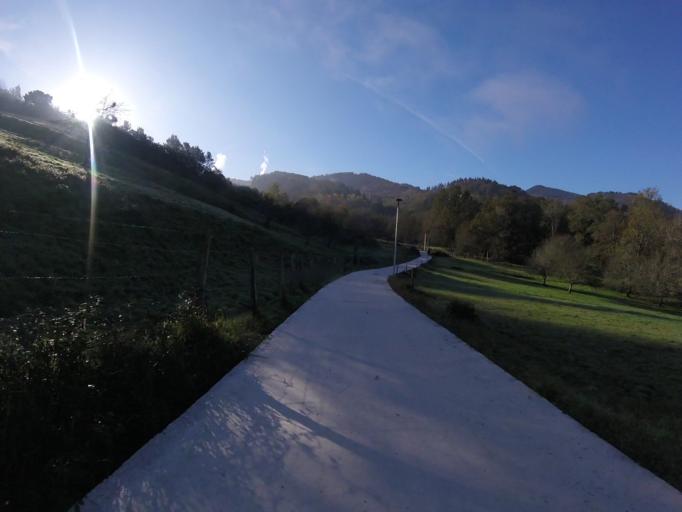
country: ES
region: Basque Country
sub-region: Provincia de Guipuzcoa
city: Usurbil
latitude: 43.2642
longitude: -2.0421
